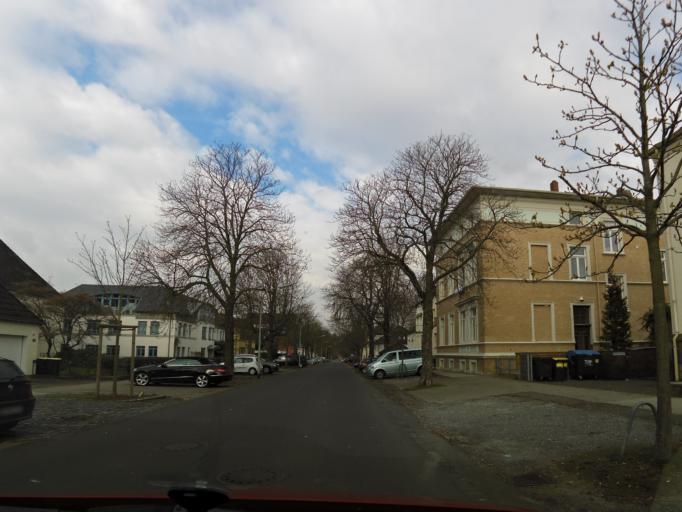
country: DE
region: Lower Saxony
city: Braunschweig
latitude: 52.2712
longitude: 10.5289
